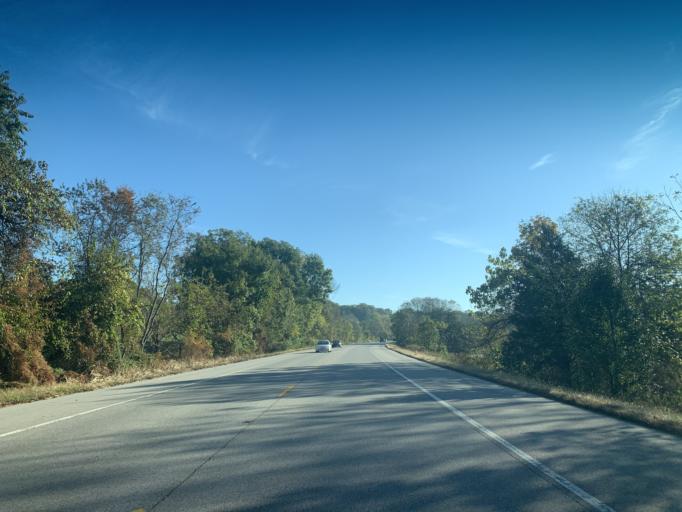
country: US
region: Maryland
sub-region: Cecil County
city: Rising Sun
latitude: 39.7079
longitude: -76.0727
